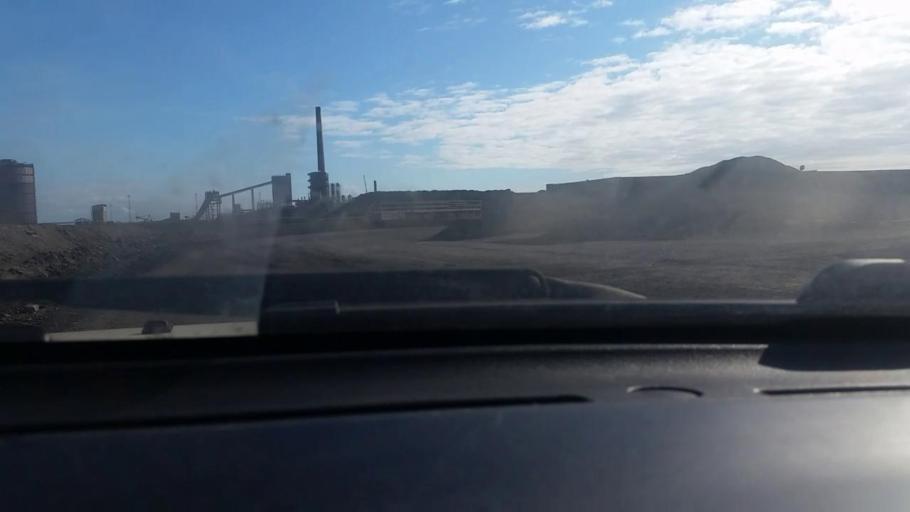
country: GB
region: Wales
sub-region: Neath Port Talbot
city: Taibach
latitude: 51.5654
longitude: -3.7765
